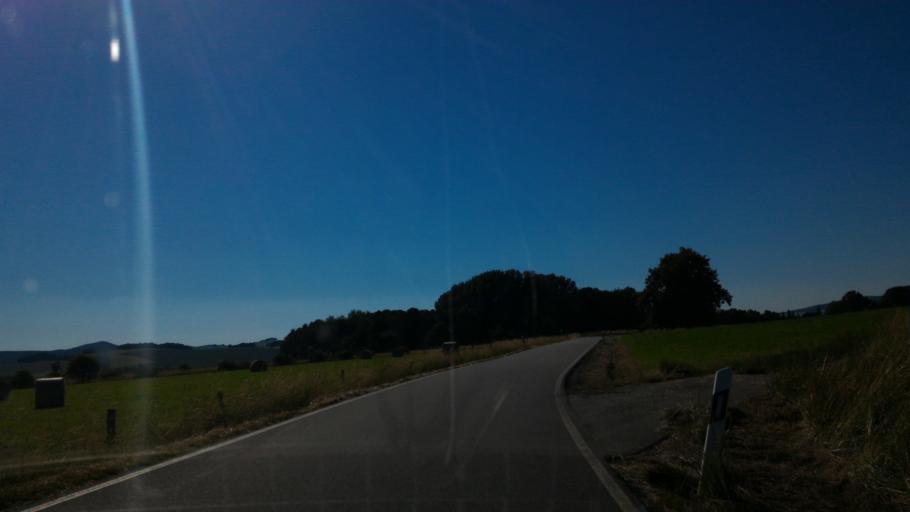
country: DE
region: Saxony
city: Mittelherwigsdorf
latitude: 50.9338
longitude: 14.7647
